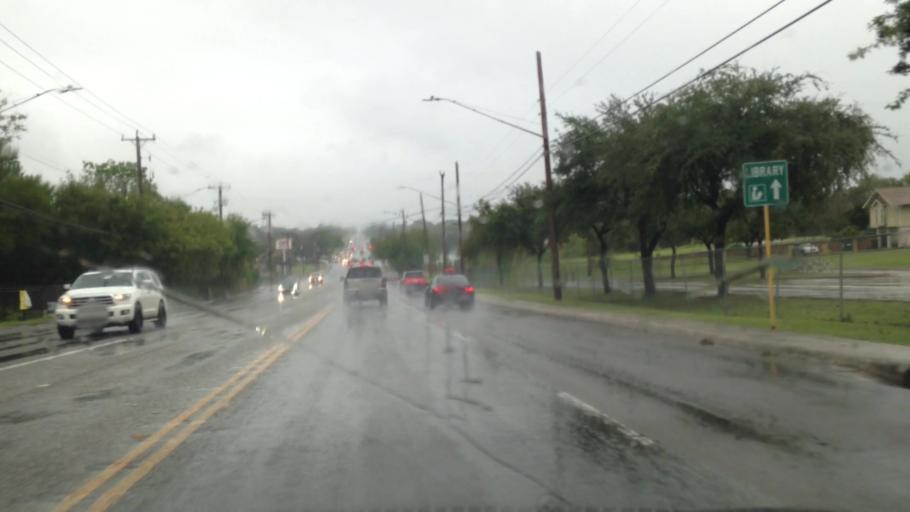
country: US
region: Texas
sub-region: Bexar County
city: Live Oak
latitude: 29.5751
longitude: -98.3705
